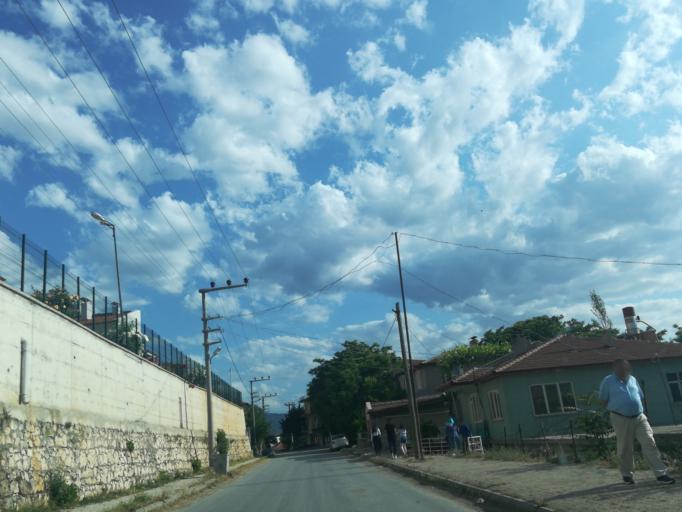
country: TR
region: Afyonkarahisar
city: Dinar
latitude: 38.0723
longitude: 30.1686
